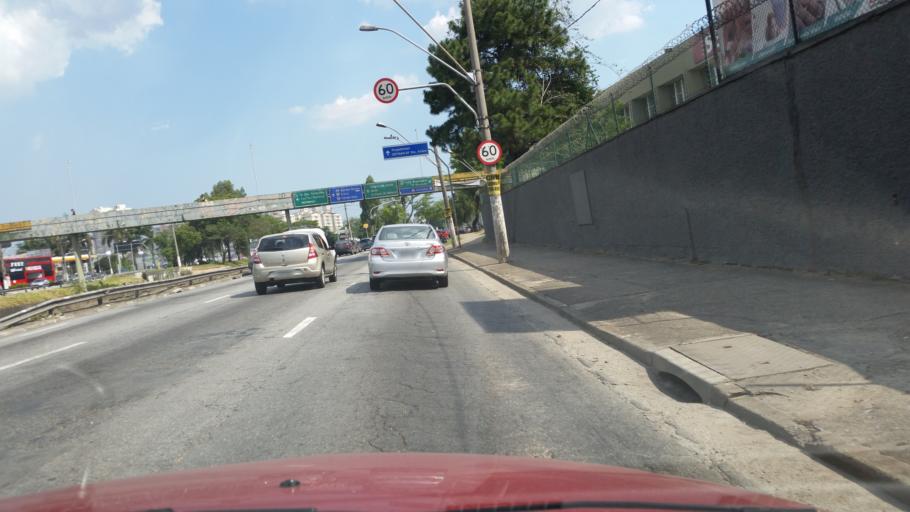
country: BR
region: Sao Paulo
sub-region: Sao Caetano Do Sul
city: Sao Caetano do Sul
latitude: -23.6366
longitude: -46.5356
